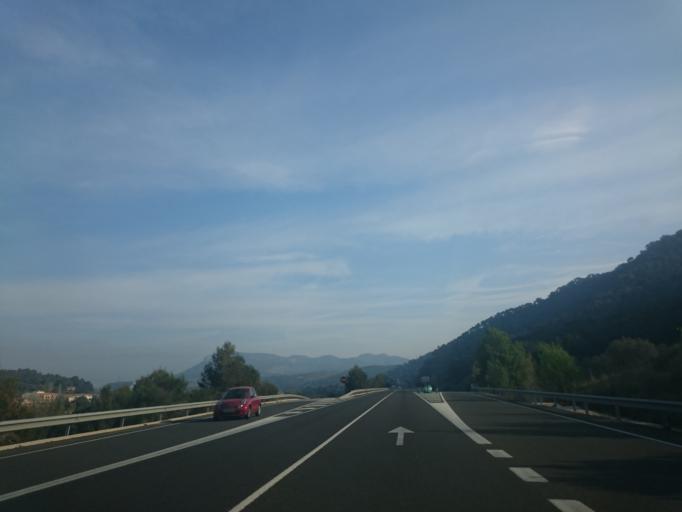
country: ES
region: Catalonia
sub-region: Provincia de Barcelona
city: Capellades
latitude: 41.5397
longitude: 1.6912
